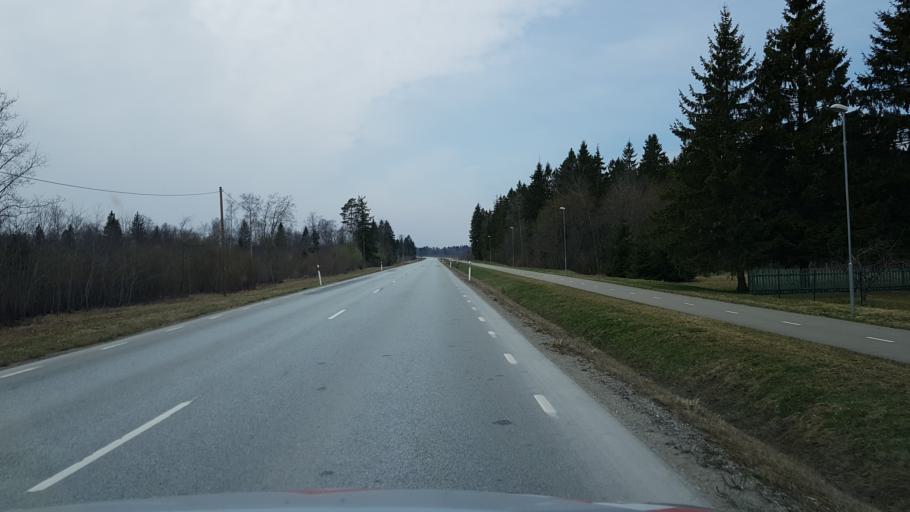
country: EE
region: Ida-Virumaa
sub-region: Kivioli linn
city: Kivioli
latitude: 59.3551
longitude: 26.8889
